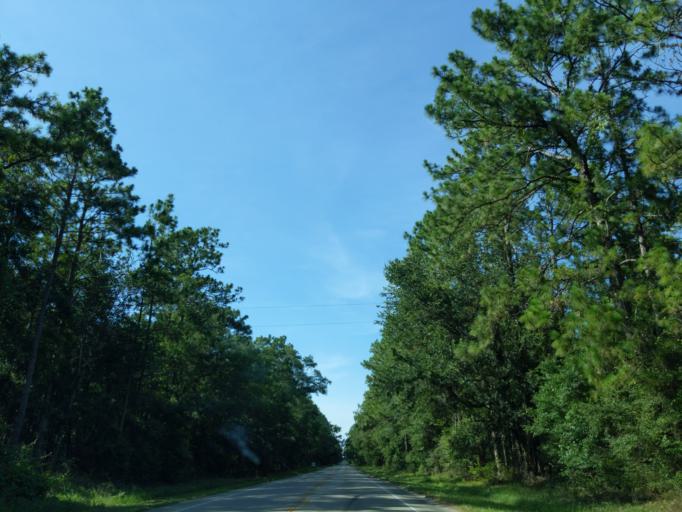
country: US
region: Florida
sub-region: Leon County
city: Woodville
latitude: 30.2960
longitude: -84.3121
